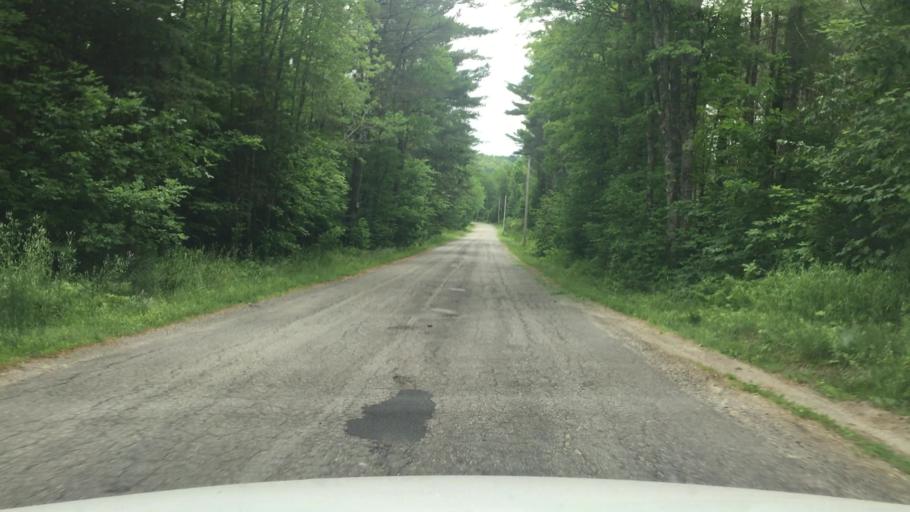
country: US
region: Maine
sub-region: Kennebec County
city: Albion
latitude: 44.4614
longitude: -69.3352
